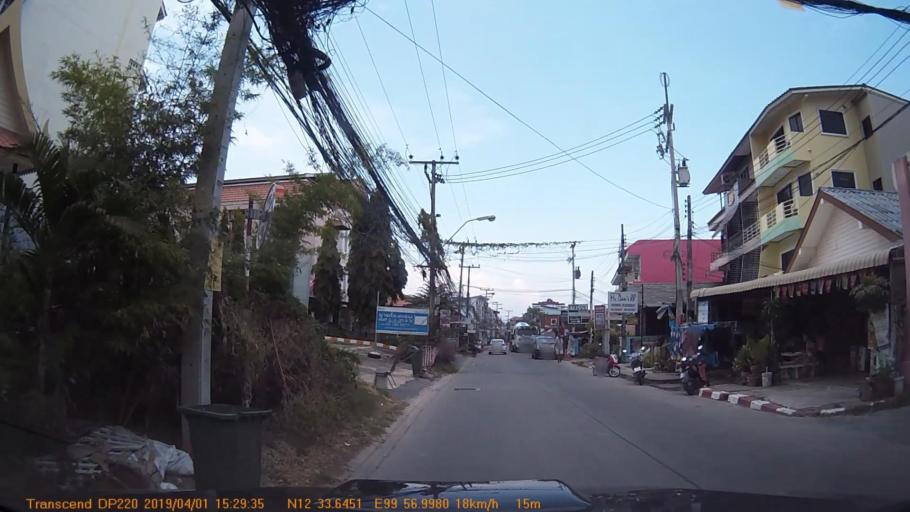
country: TH
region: Prachuap Khiri Khan
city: Hua Hin
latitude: 12.5608
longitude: 99.9501
